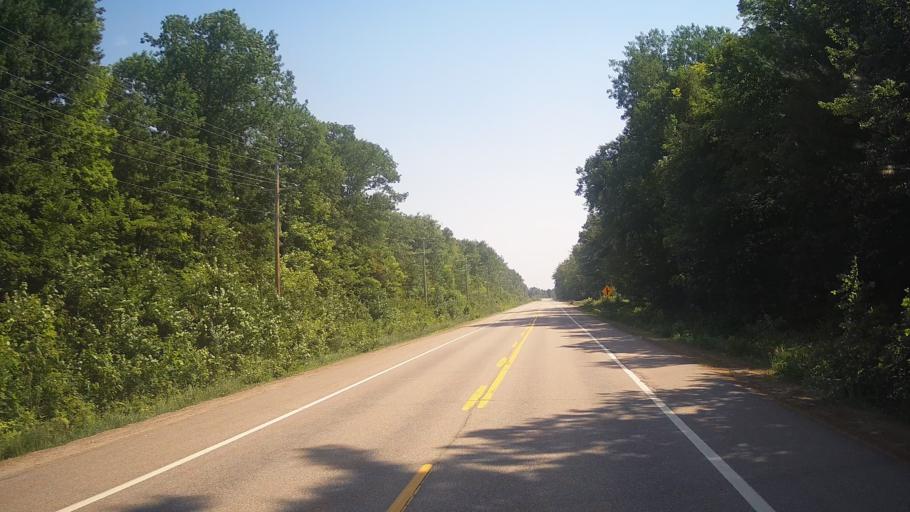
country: CA
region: Ontario
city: Pembroke
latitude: 45.8396
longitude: -77.0134
